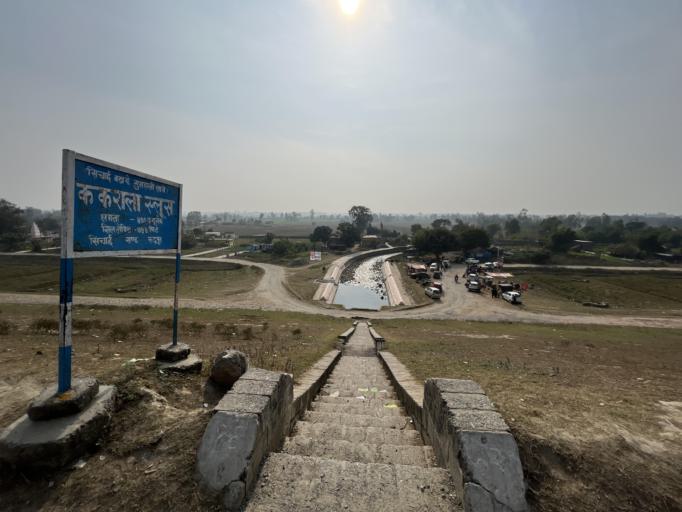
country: IN
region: Uttarakhand
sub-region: Naini Tal
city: Kaladhungi
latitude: 29.1220
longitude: 79.2837
